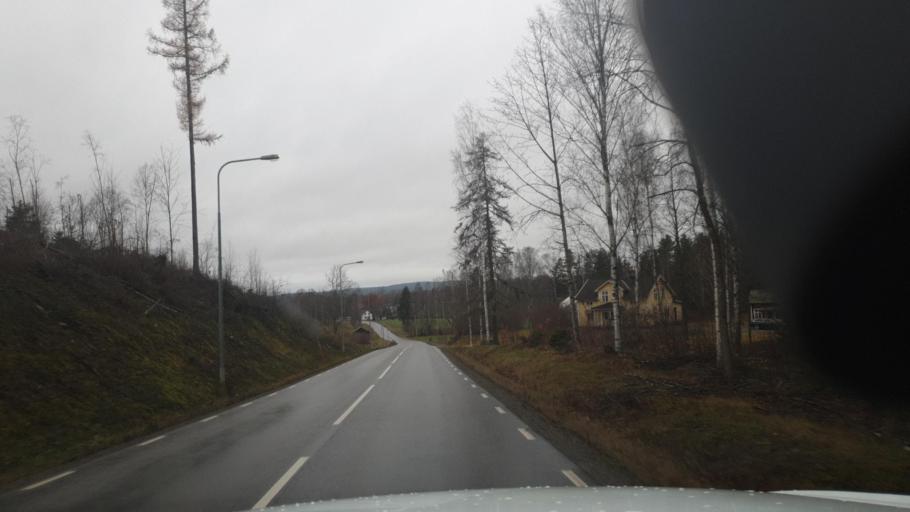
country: SE
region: Vaermland
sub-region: Arvika Kommun
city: Arvika
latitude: 59.5448
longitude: 12.5730
